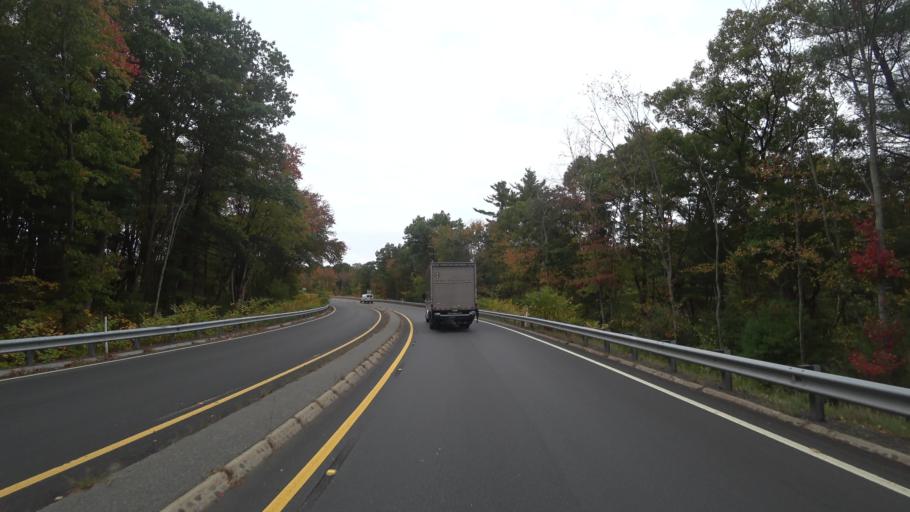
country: US
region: Massachusetts
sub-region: Middlesex County
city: Wilmington
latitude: 42.5838
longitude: -71.1546
